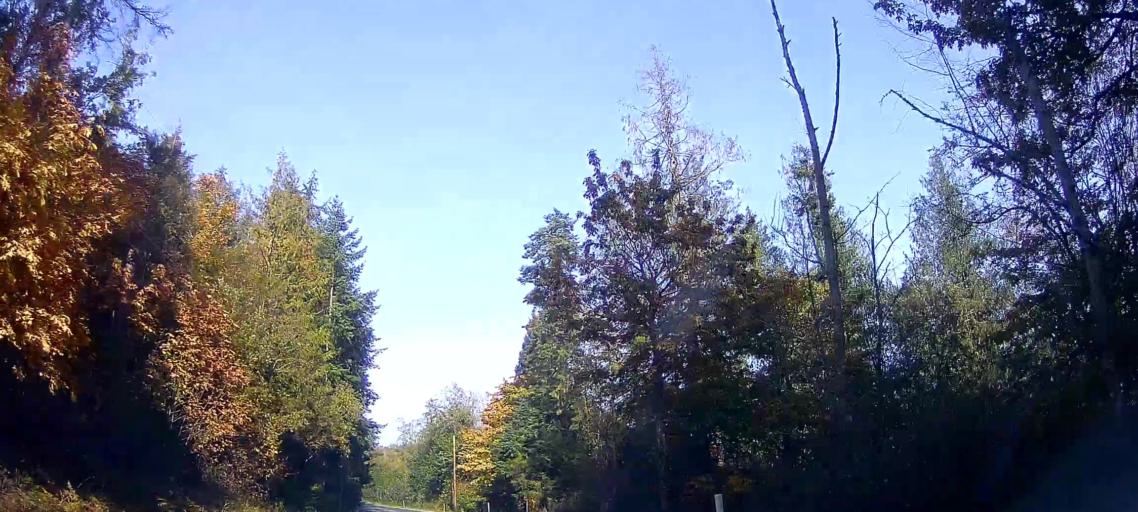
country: US
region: Washington
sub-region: Snohomish County
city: Stanwood
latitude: 48.2360
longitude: -122.4560
